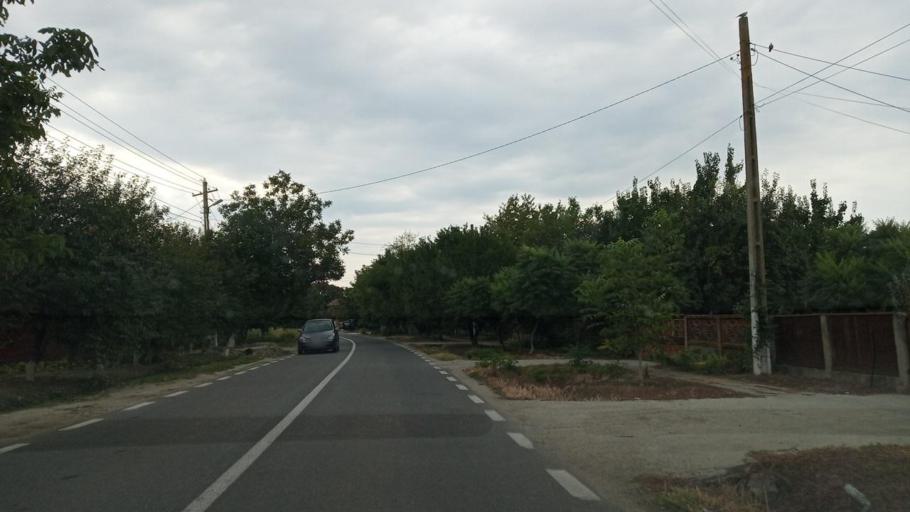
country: RO
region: Giurgiu
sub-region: Comuna Izvoarele
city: Isvoarele
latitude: 44.1708
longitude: 26.3249
